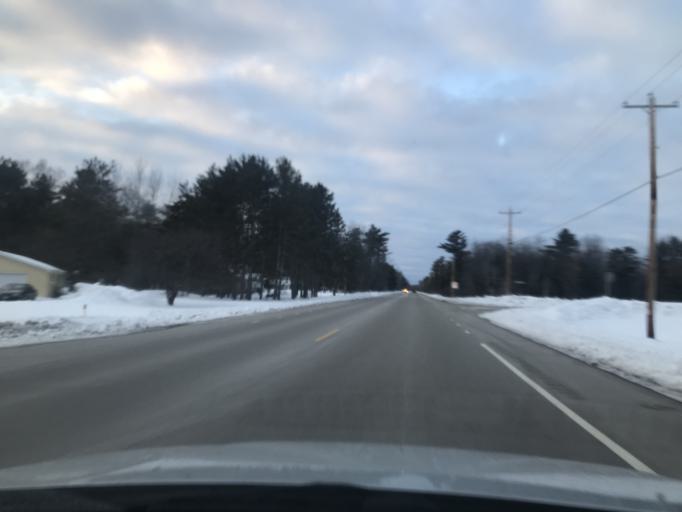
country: US
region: Wisconsin
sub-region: Marinette County
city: Marinette
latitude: 45.1429
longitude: -87.6947
